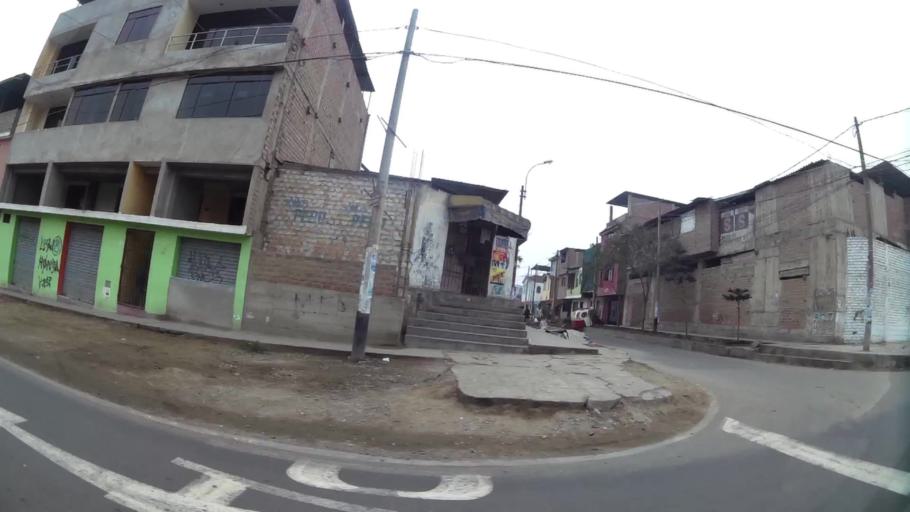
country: PE
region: Lima
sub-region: Lima
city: Surco
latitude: -12.1748
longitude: -76.9443
